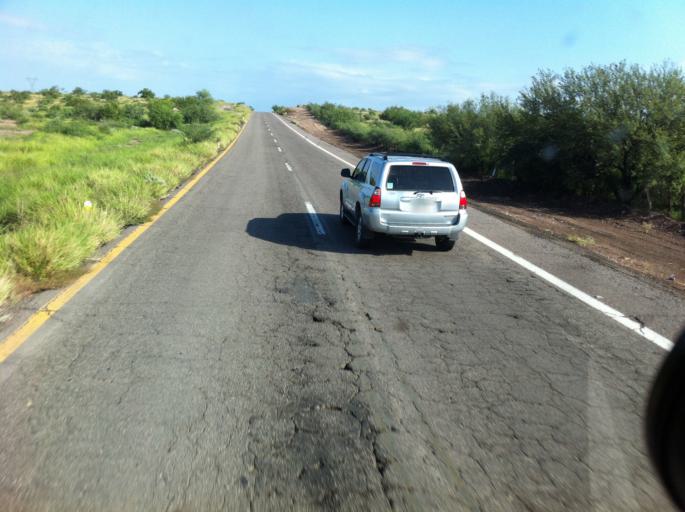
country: MX
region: Sonora
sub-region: Hermosillo
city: Miguel Aleman (La Doce)
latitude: 28.5162
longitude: -111.0457
